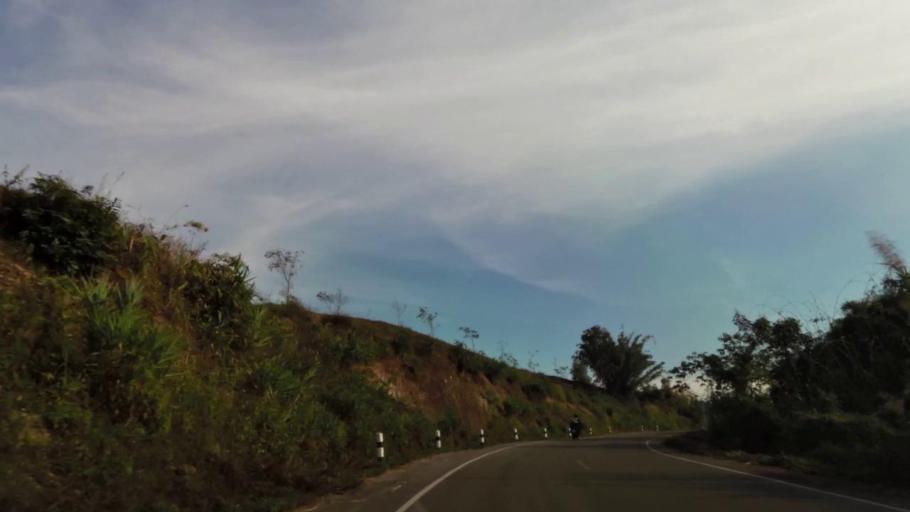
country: TH
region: Chiang Rai
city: Khun Tan
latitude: 19.8639
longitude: 100.3664
